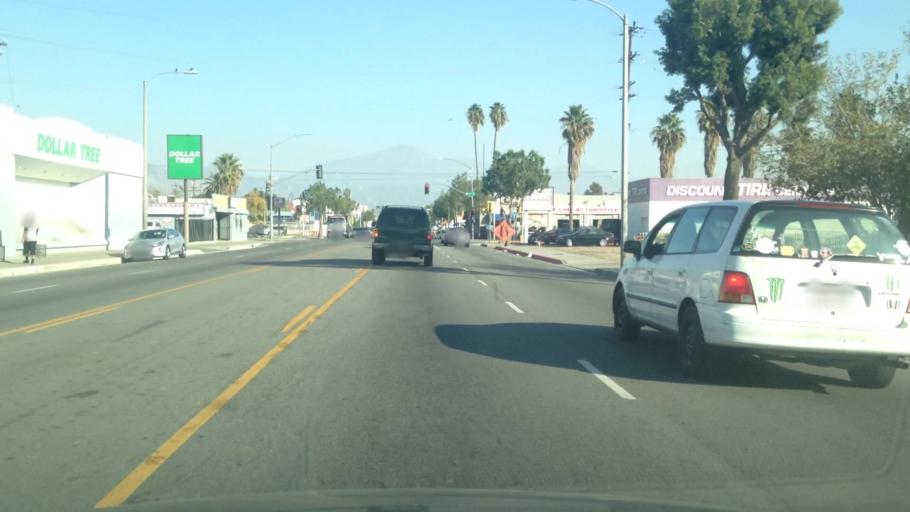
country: US
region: California
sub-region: San Bernardino County
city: San Bernardino
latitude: 34.1213
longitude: -117.2863
